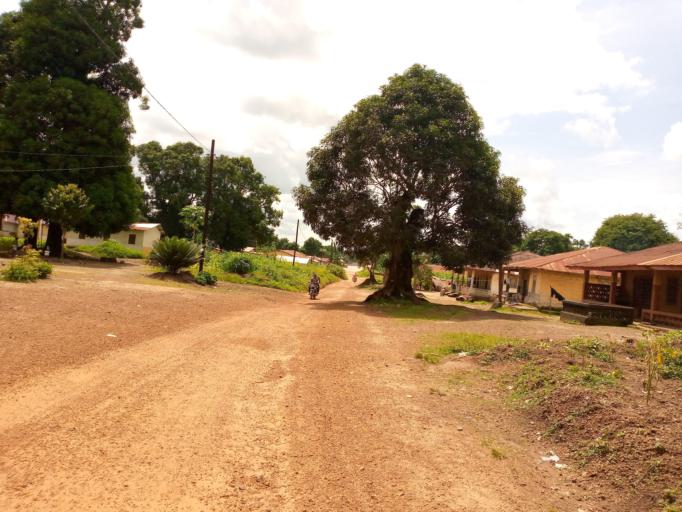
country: SL
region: Northern Province
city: Magburaka
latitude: 8.7128
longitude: -11.9356
